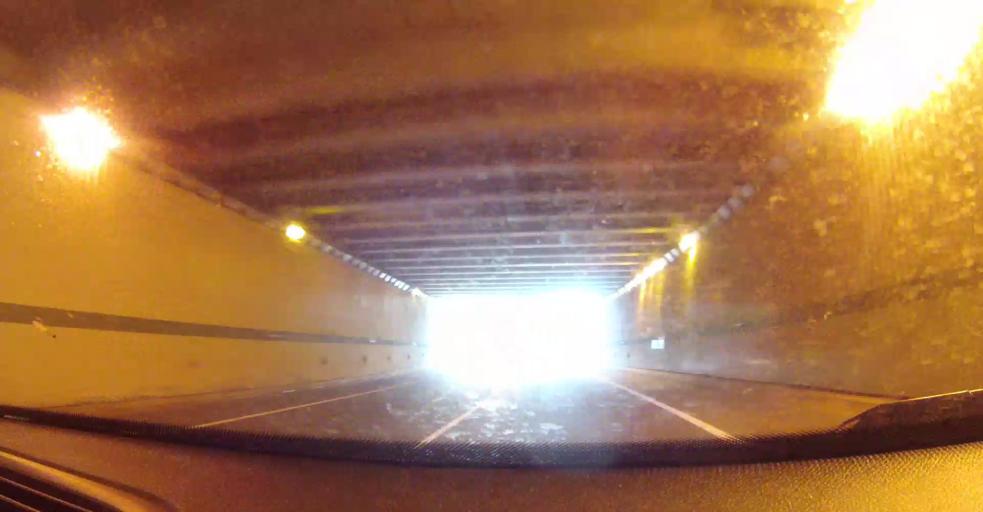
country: ES
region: Asturias
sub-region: Province of Asturias
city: Cangas de Onis
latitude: 43.3569
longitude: -5.1317
